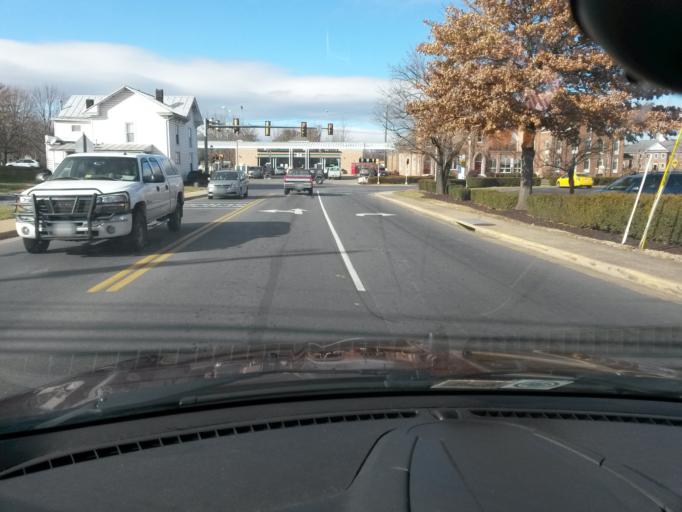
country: US
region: Virginia
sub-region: Rockingham County
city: Bridgewater
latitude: 38.3834
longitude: -78.9742
